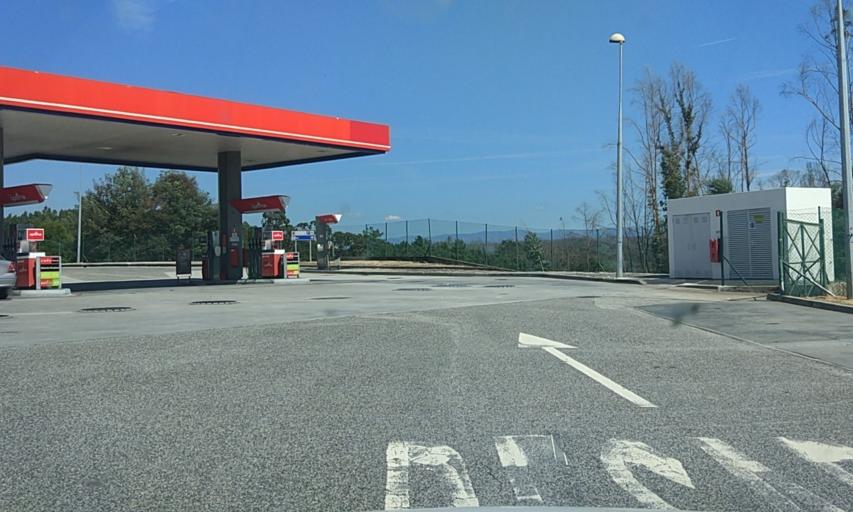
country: PT
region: Viseu
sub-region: Santa Comba Dao
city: Santa Comba Dao
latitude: 40.3487
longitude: -8.1728
